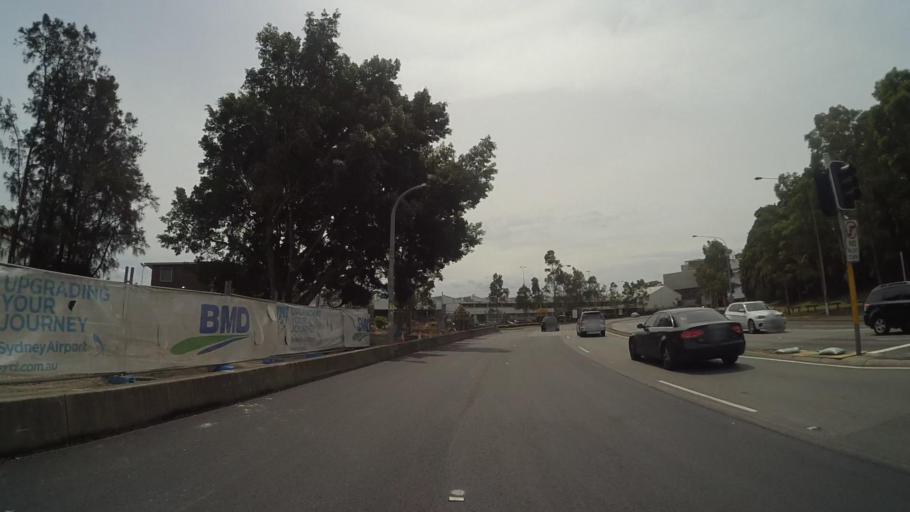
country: AU
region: New South Wales
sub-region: Botany Bay
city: Mascot
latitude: -33.9314
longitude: 151.1843
